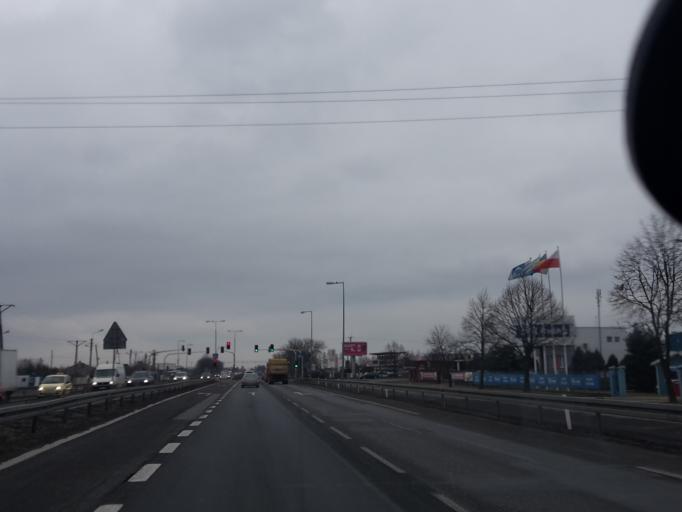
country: PL
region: Masovian Voivodeship
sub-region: Powiat warszawski zachodni
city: Dziekanow Lesny
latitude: 52.3589
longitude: 20.8311
